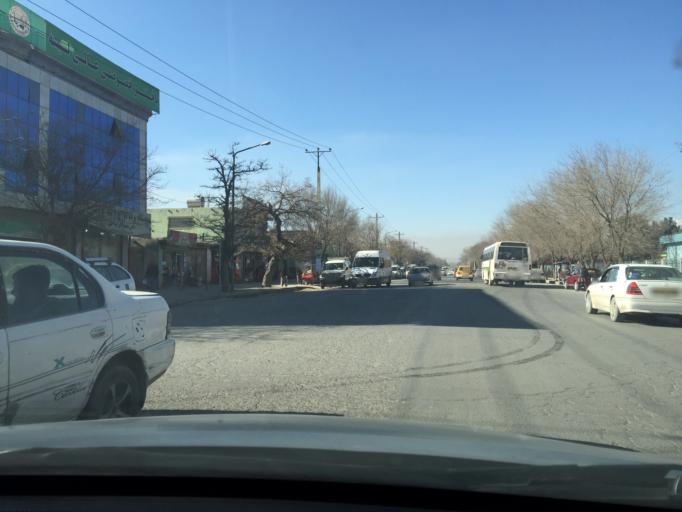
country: AF
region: Kabul
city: Kabul
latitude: 34.5111
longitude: 69.1403
